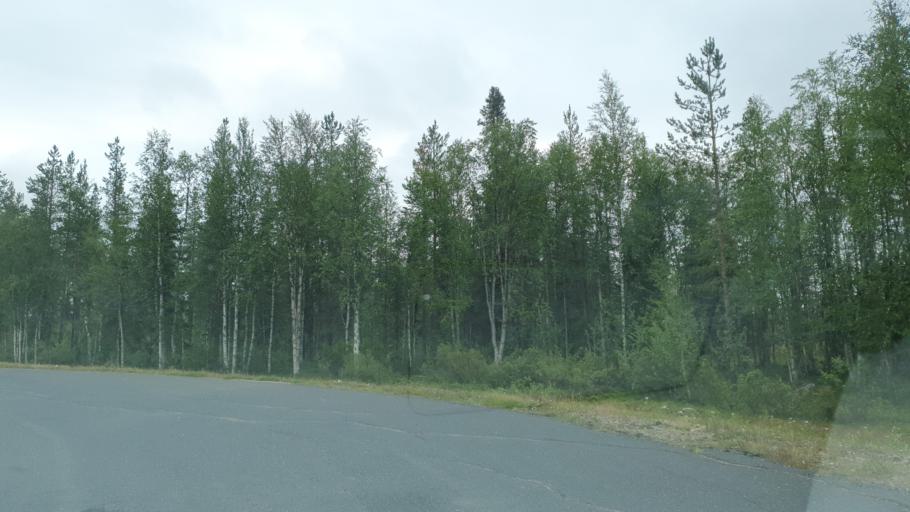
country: FI
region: Lapland
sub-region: Pohjois-Lappi
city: Sodankylae
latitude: 67.4234
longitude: 26.4409
